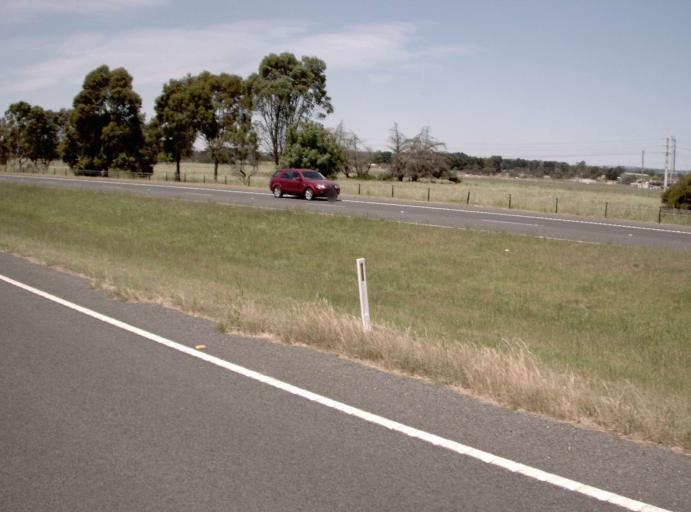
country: AU
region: Victoria
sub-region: Latrobe
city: Morwell
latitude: -38.2441
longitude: 146.4402
